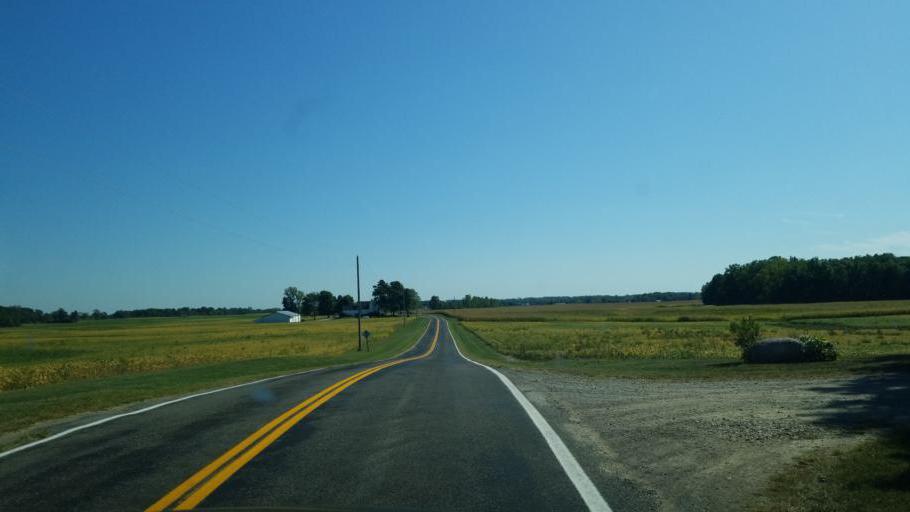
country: US
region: Ohio
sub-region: Champaign County
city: Mechanicsburg
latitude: 40.1439
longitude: -83.6015
